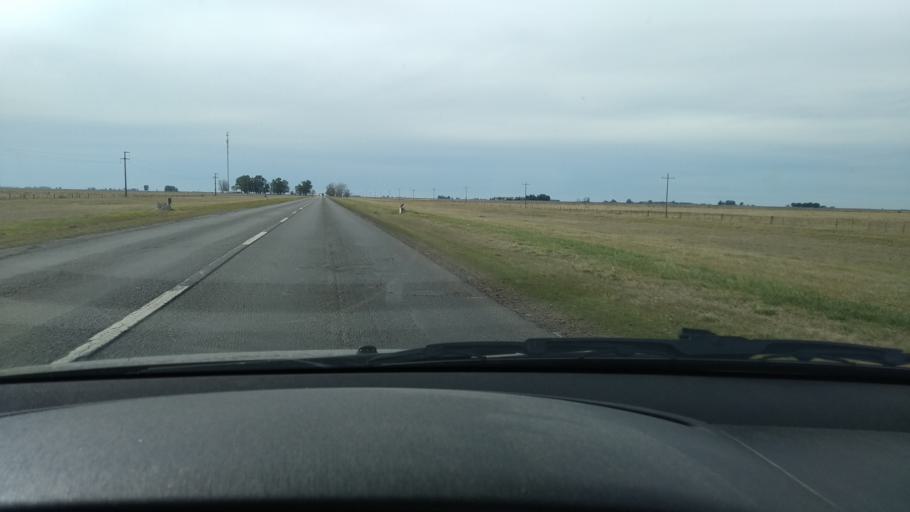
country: AR
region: Buenos Aires
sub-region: Partido de Azul
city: Azul
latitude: -36.7390
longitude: -59.7893
